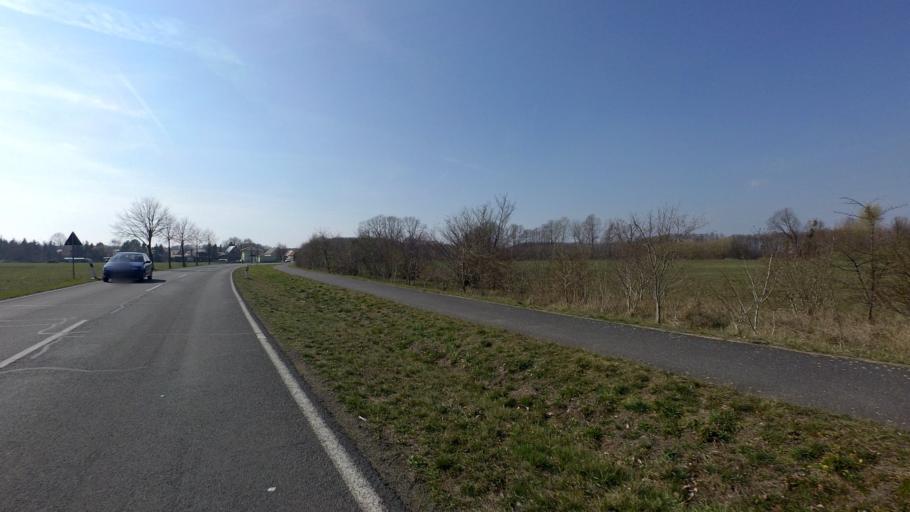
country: DE
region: Brandenburg
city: Golssen
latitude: 51.9641
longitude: 13.5932
